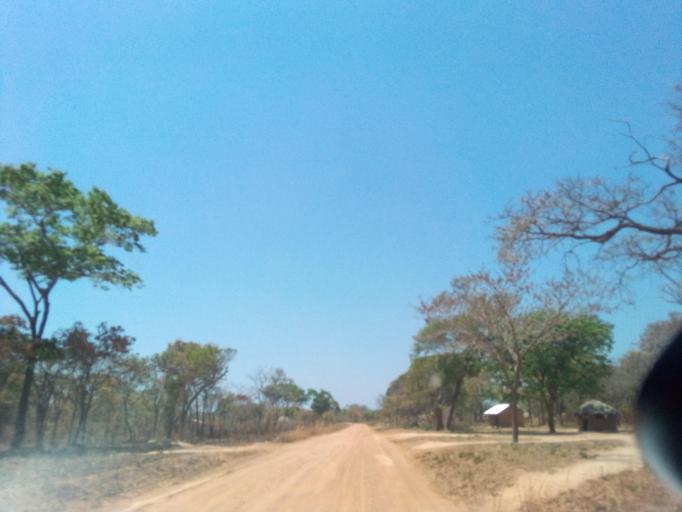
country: ZM
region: Northern
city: Mpika
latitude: -12.2514
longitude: 30.6737
